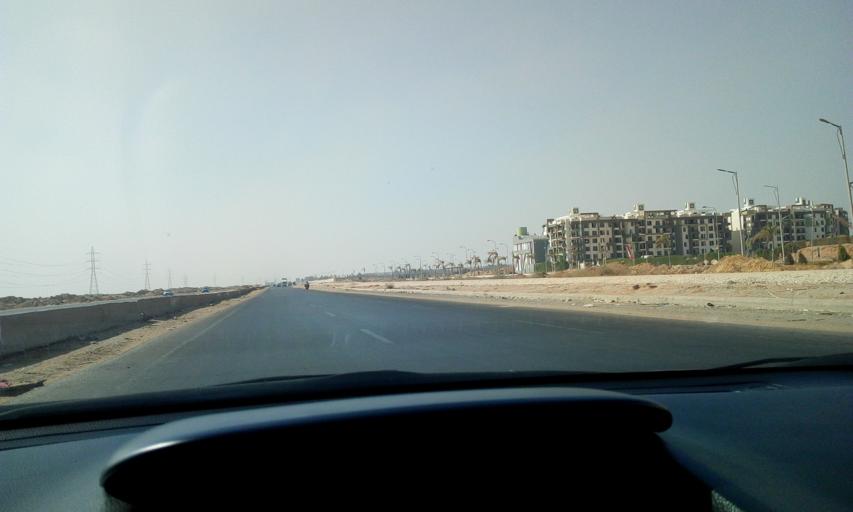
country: EG
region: Al Jizah
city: Madinat Sittah Uktubar
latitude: 29.8930
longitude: 31.0826
